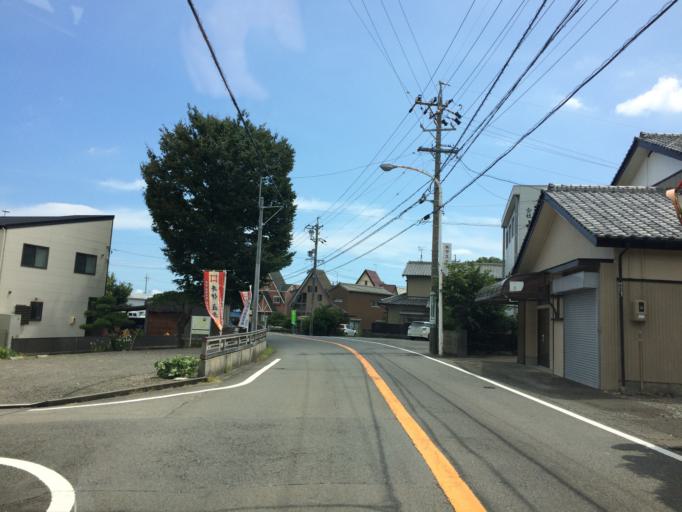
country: JP
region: Shizuoka
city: Yaizu
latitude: 34.8823
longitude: 138.3135
